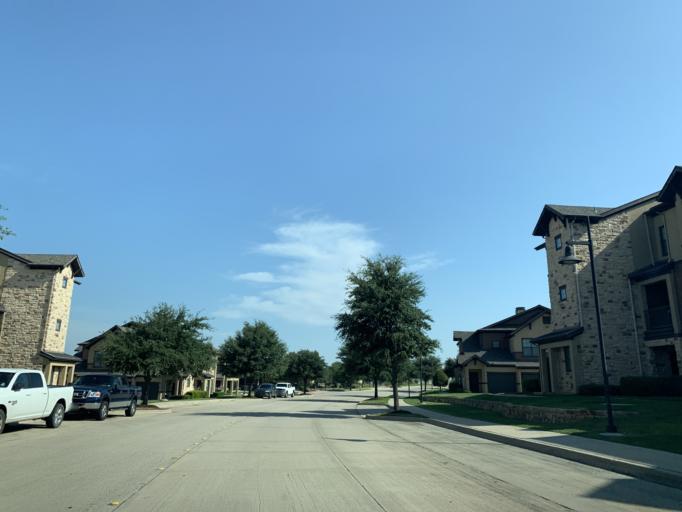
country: US
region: Texas
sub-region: Tarrant County
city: Blue Mound
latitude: 32.8936
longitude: -97.3121
